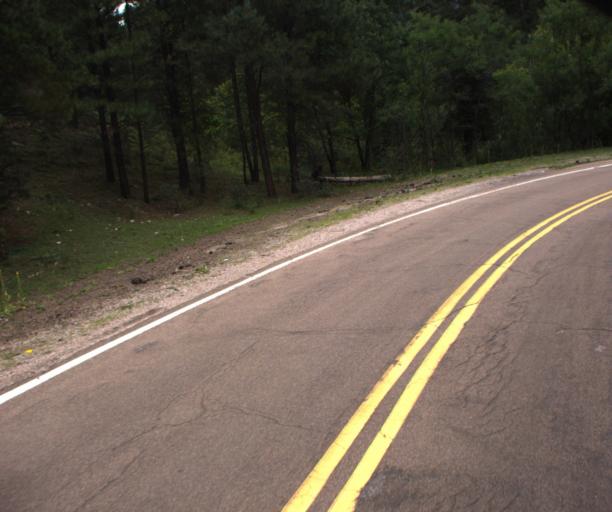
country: US
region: Arizona
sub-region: Navajo County
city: Pinetop-Lakeside
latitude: 34.0306
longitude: -109.7504
